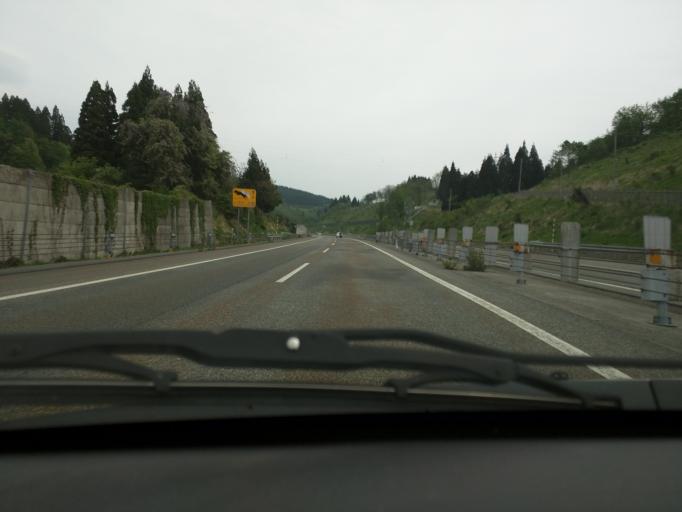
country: JP
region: Niigata
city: Ojiya
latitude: 37.2824
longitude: 138.7872
